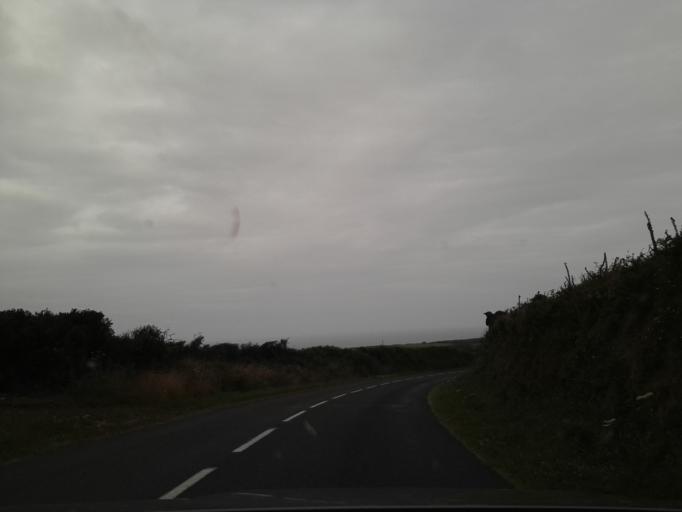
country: FR
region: Lower Normandy
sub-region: Departement de la Manche
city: Beaumont-Hague
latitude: 49.6977
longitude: -1.9252
